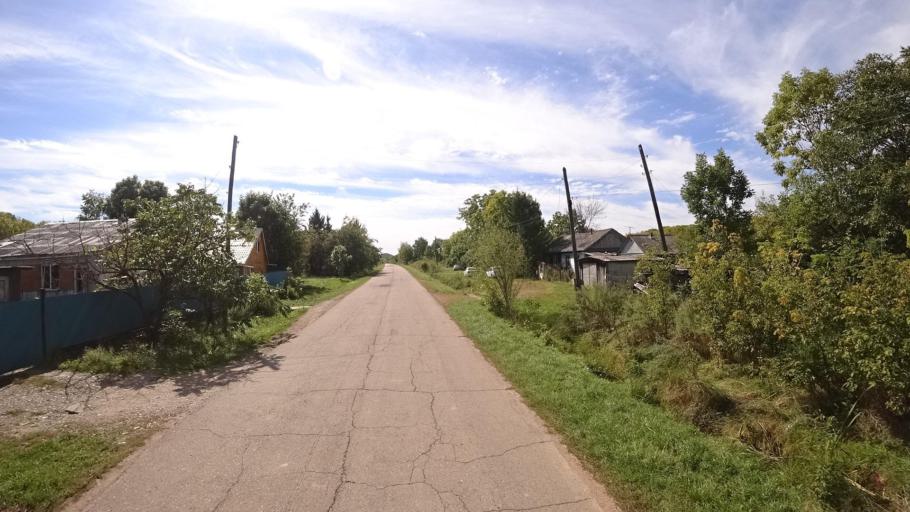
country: RU
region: Primorskiy
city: Kirovskiy
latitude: 44.7568
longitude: 133.6070
